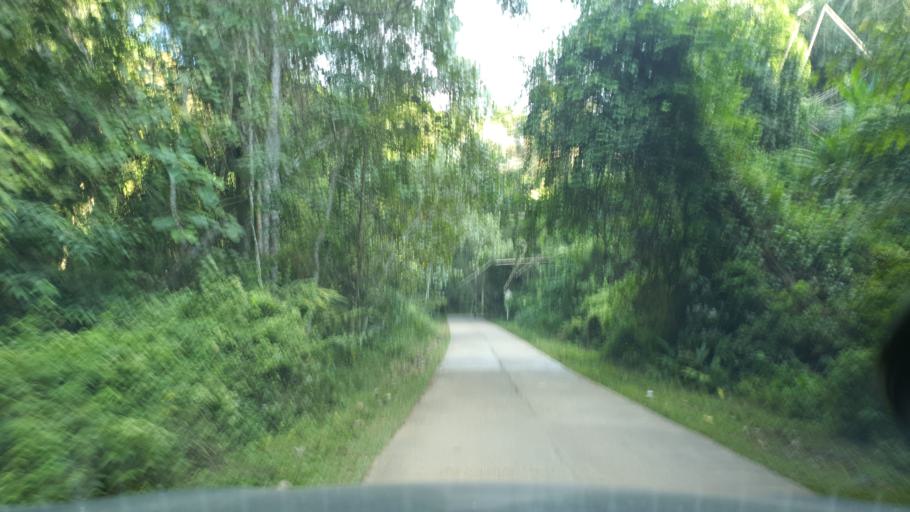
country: TH
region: Chiang Mai
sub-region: Amphoe Chiang Dao
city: Chiang Dao
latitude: 19.4118
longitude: 98.7978
